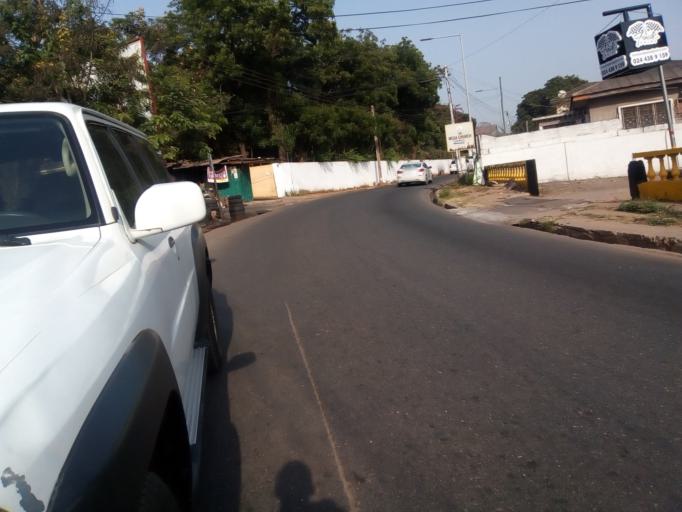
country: GH
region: Greater Accra
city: Accra
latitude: 5.5851
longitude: -0.2157
